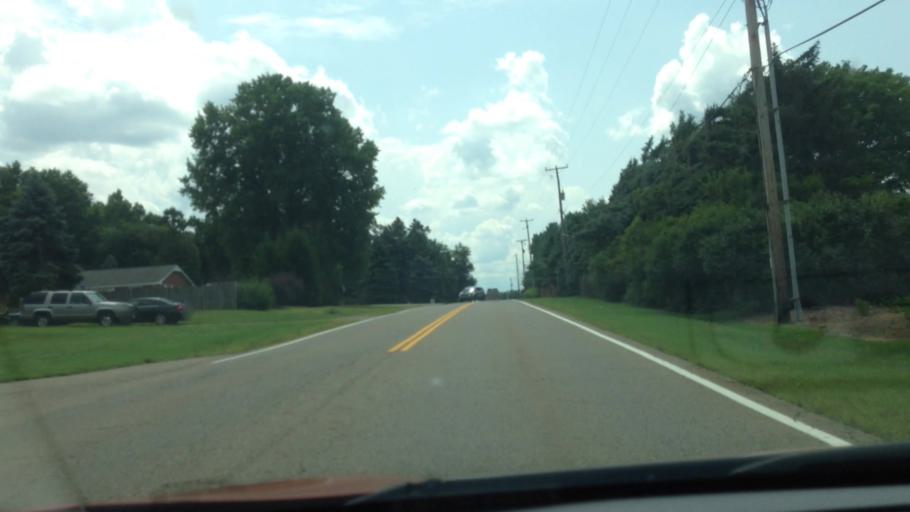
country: US
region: Ohio
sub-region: Stark County
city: Perry Heights
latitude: 40.8295
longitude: -81.4631
